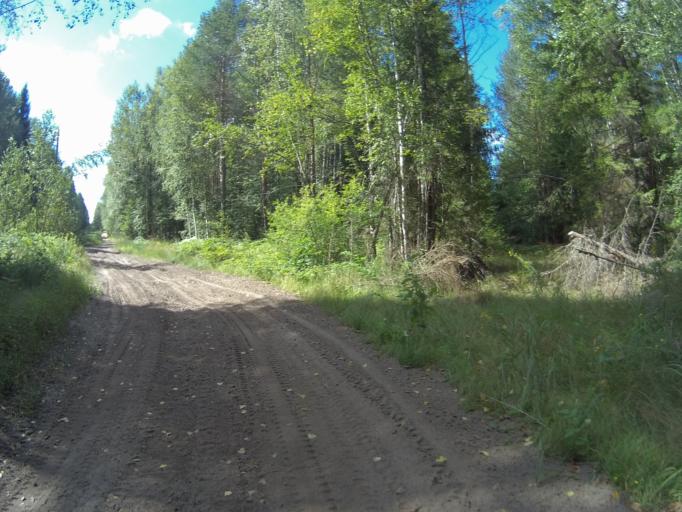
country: RU
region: Vladimir
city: Raduzhnyy
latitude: 55.9033
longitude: 40.1990
